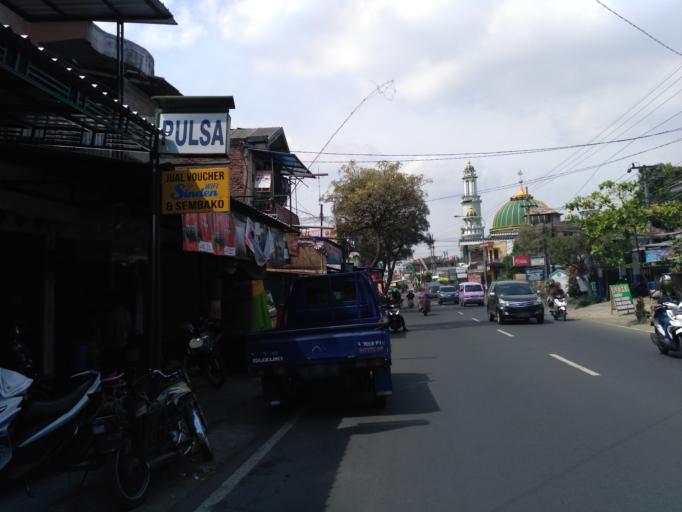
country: ID
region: East Java
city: Malang
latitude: -7.9185
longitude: 112.5903
